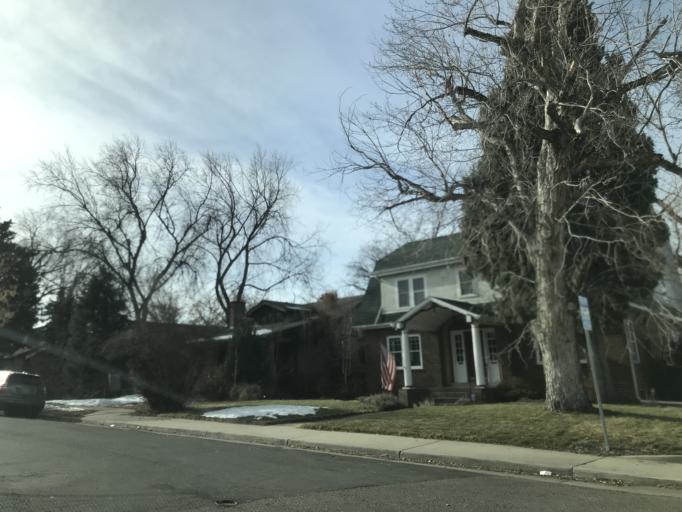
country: US
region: Colorado
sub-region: Arapahoe County
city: Littleton
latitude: 39.6151
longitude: -105.0102
